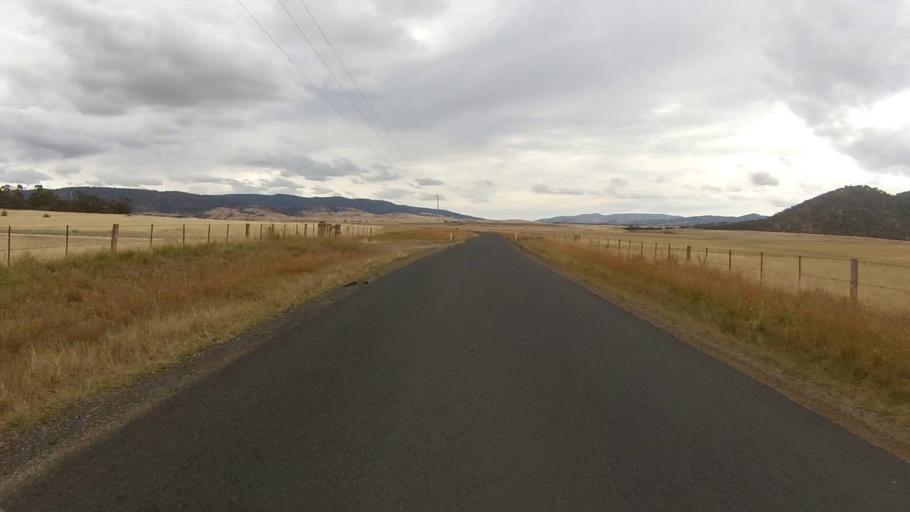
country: AU
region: Tasmania
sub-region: Northern Midlands
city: Evandale
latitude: -41.8250
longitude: 147.7998
